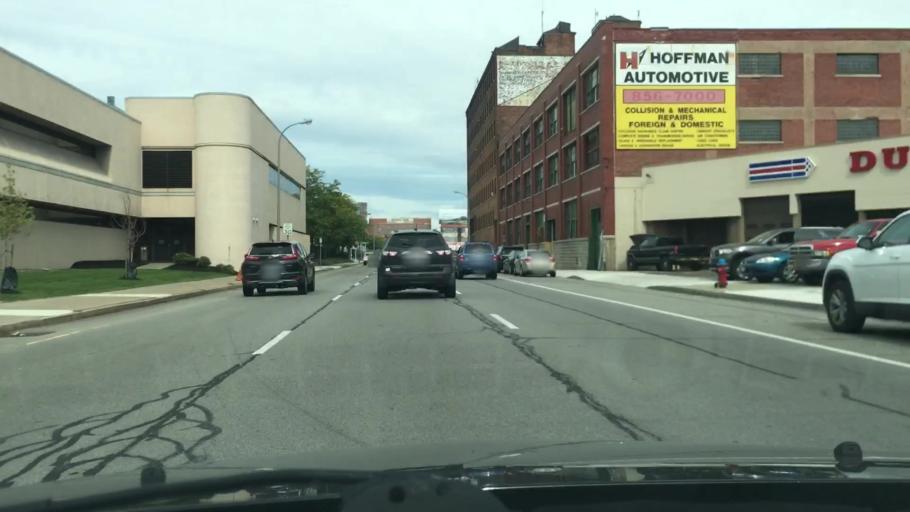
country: US
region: New York
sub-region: Erie County
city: Buffalo
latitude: 42.8868
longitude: -78.8689
